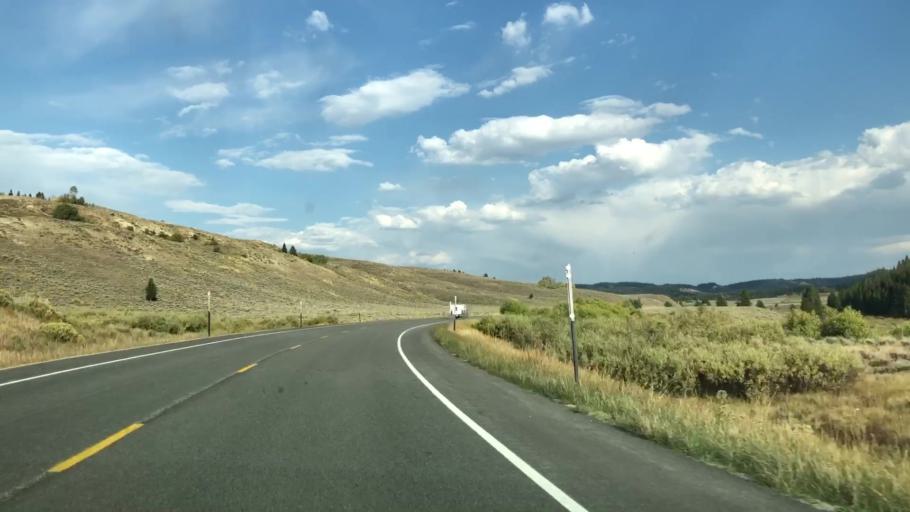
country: US
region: Wyoming
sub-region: Sublette County
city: Pinedale
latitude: 43.1523
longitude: -110.2842
